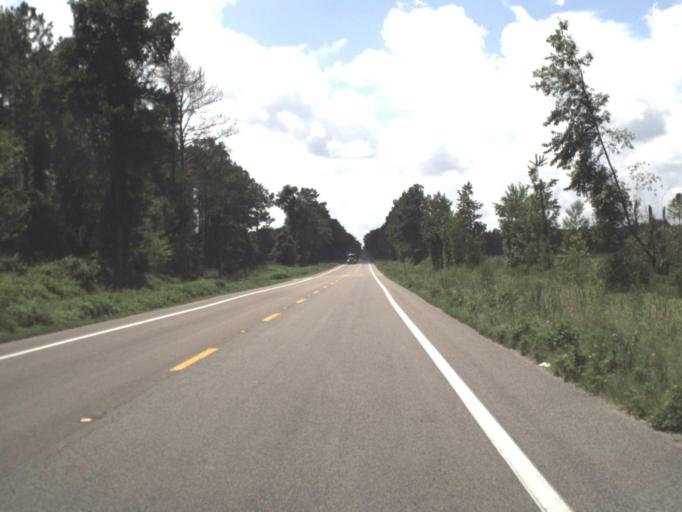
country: US
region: Florida
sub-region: Gilchrist County
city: Trenton
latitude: 29.6451
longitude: -82.8350
